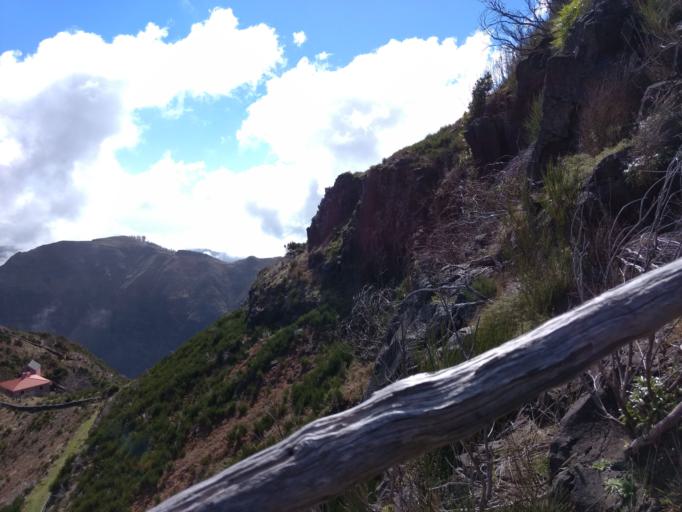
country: PT
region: Madeira
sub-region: Sao Vicente
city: Sao Vicente
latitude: 32.7376
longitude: -17.0488
